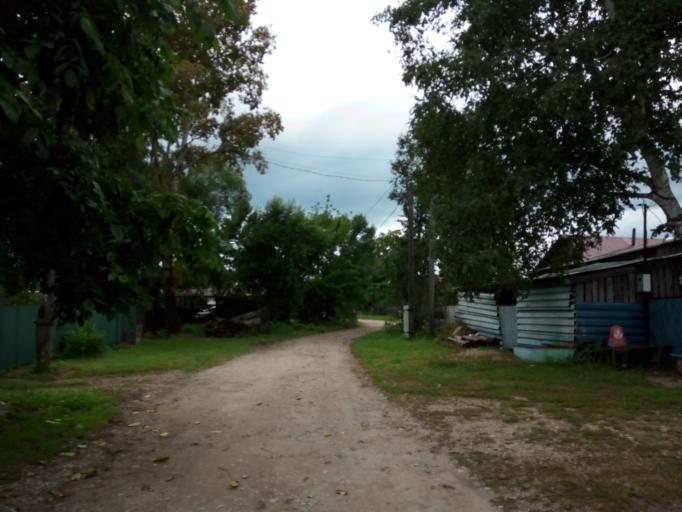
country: RU
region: Primorskiy
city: Dal'nerechensk
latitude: 45.9351
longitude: 133.8182
